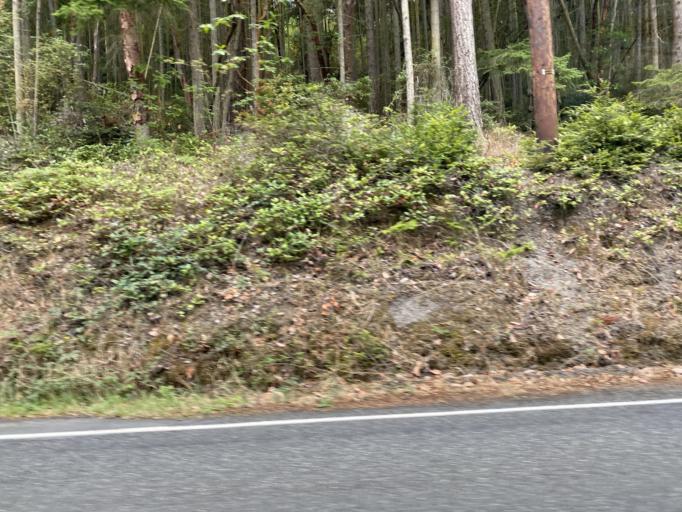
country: US
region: Washington
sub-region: Island County
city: Coupeville
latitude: 48.2145
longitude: -122.7242
